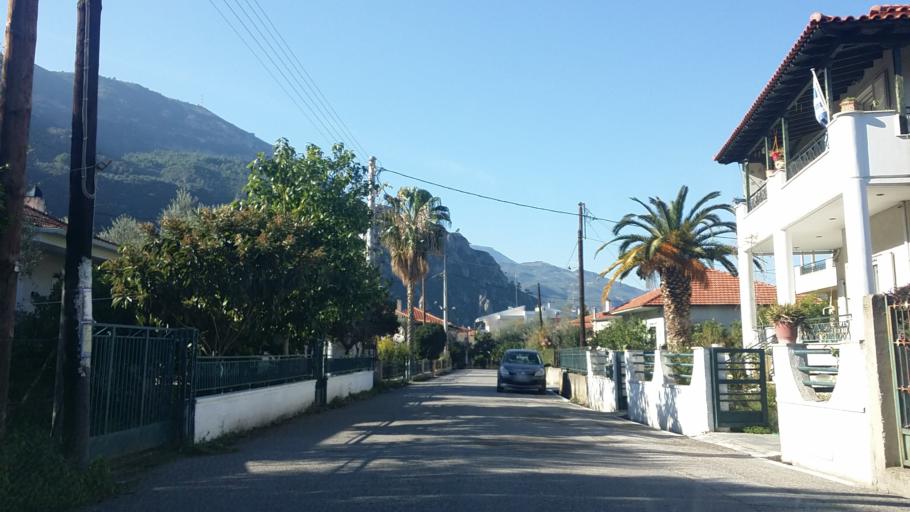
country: GR
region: West Greece
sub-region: Nomos Achaias
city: Temeni
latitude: 38.1869
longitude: 22.1867
